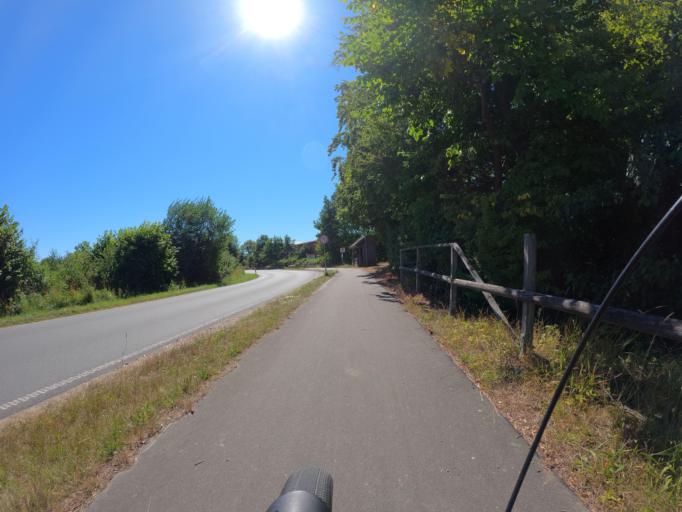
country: DE
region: Schleswig-Holstein
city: Dollerup
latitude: 54.7916
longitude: 9.7237
